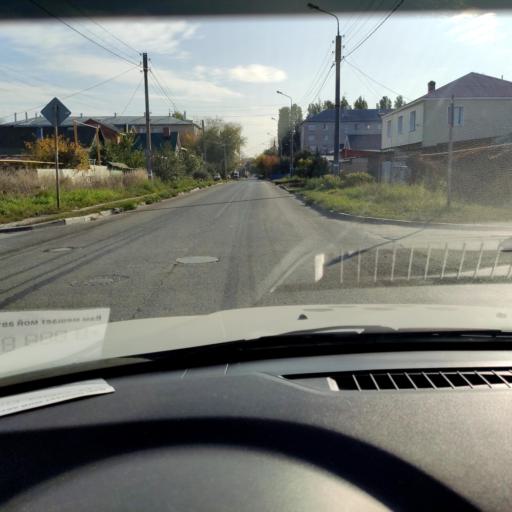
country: RU
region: Samara
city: Tol'yatti
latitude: 53.5259
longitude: 49.4260
